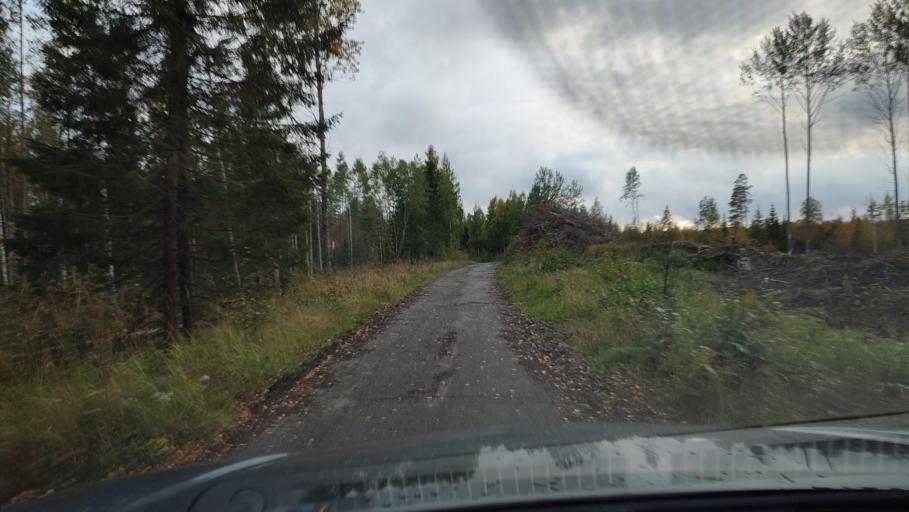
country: FI
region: Ostrobothnia
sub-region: Sydosterbotten
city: Kristinestad
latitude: 62.2715
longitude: 21.4360
